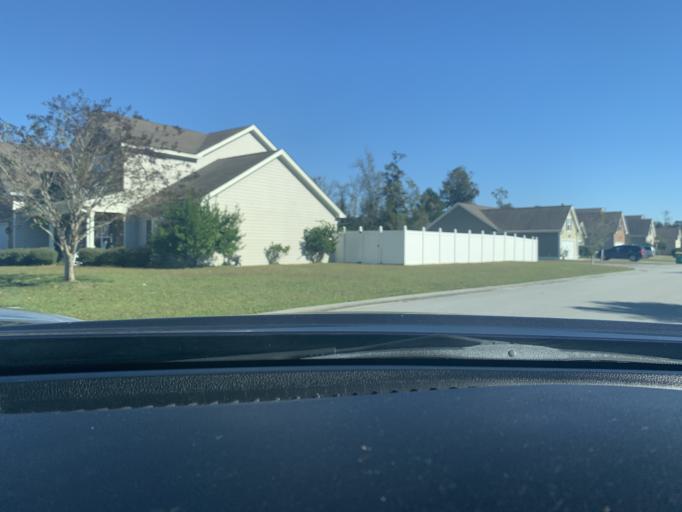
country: US
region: Georgia
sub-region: Chatham County
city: Pooler
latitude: 32.0732
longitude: -81.2687
